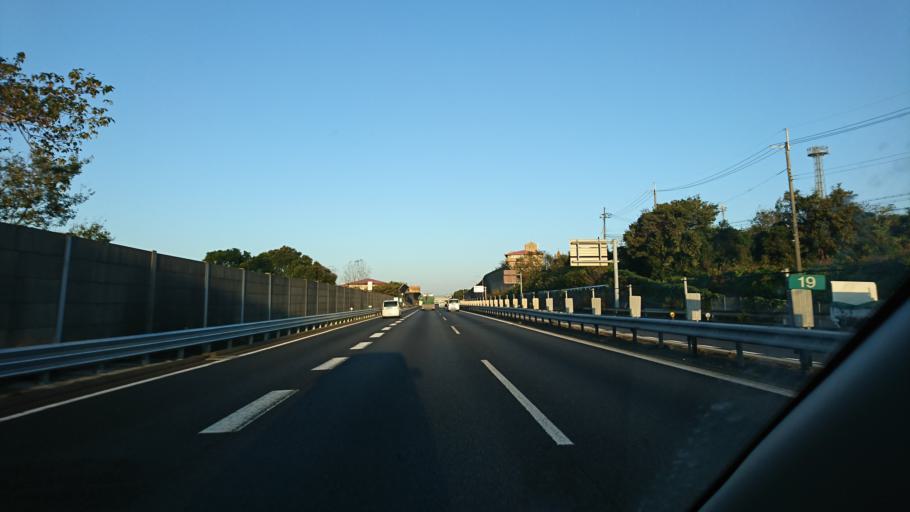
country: JP
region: Hyogo
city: Akashi
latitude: 34.7071
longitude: 134.9499
